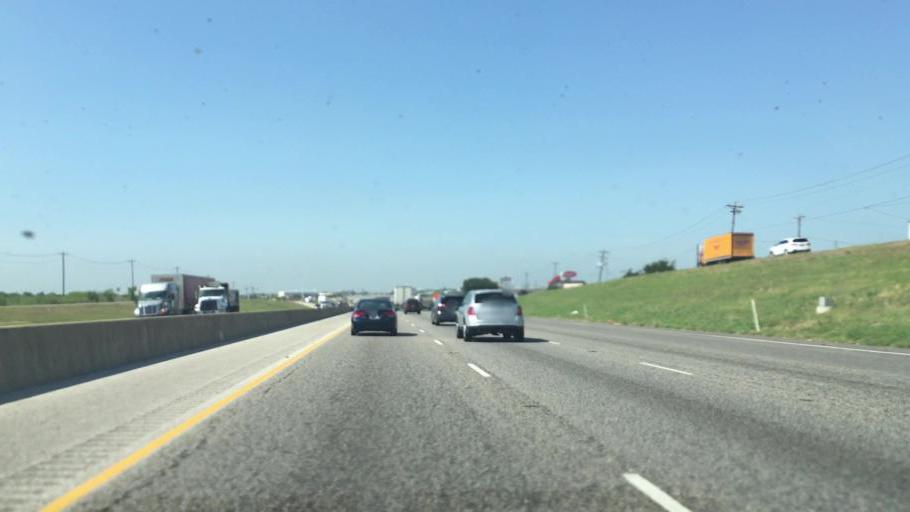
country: US
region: Texas
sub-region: Hays County
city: Buda
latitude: 30.0654
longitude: -97.8310
